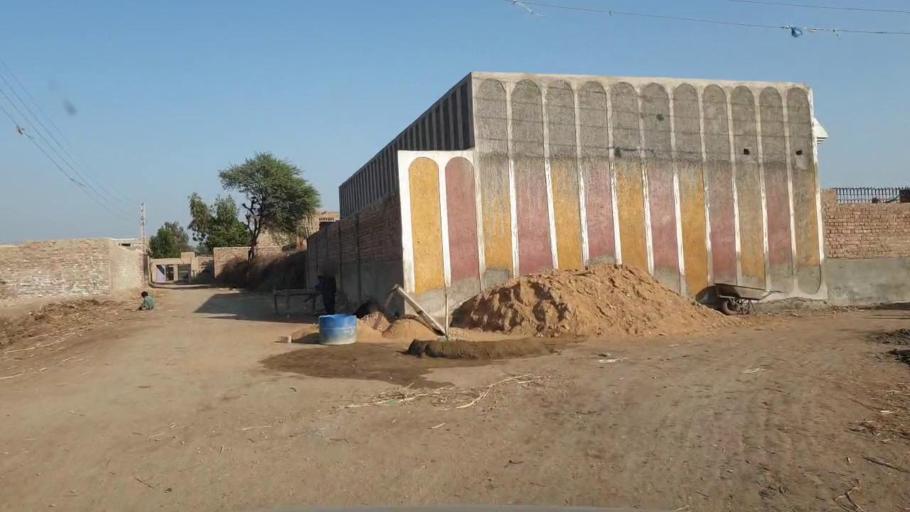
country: PK
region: Sindh
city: Tando Allahyar
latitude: 25.3568
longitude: 68.7035
